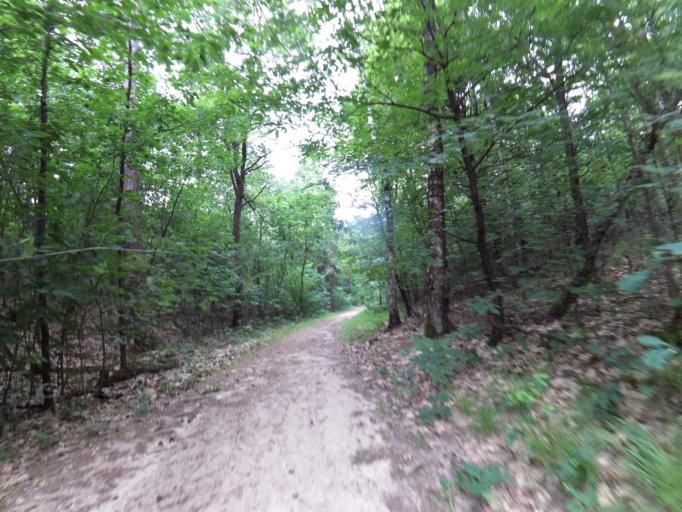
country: NL
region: North Brabant
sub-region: Gemeente Cuijk
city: Cuijk
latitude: 51.7621
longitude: 5.8926
